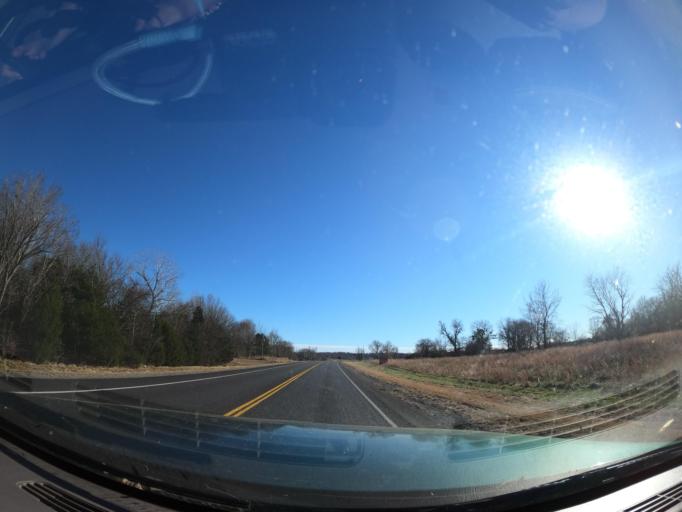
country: US
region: Oklahoma
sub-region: McIntosh County
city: Eufaula
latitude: 35.2628
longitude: -95.5802
